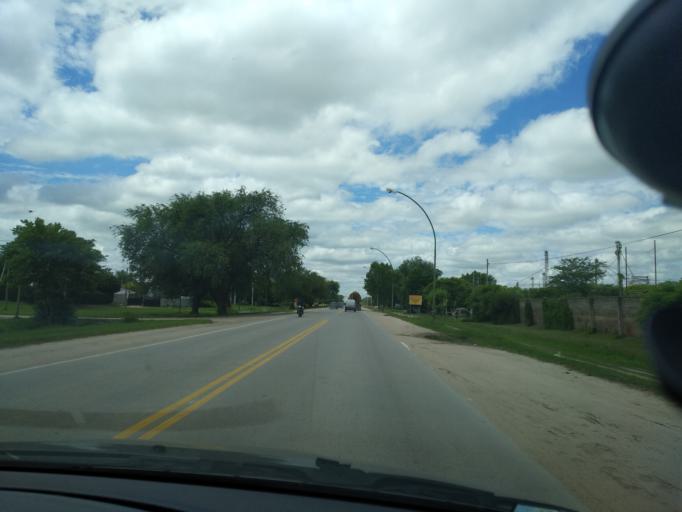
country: AR
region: Cordoba
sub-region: Departamento de Rio Segundo
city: Rio Segundo
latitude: -31.6459
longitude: -63.9033
